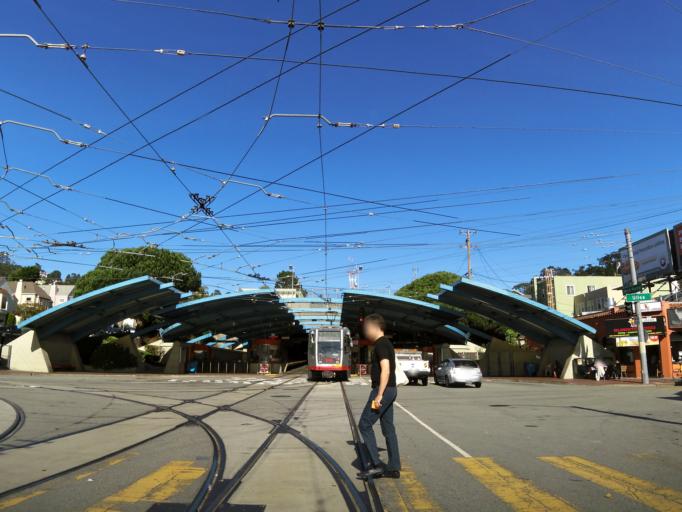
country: US
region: California
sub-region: San Mateo County
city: Daly City
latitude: 37.7408
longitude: -122.4659
